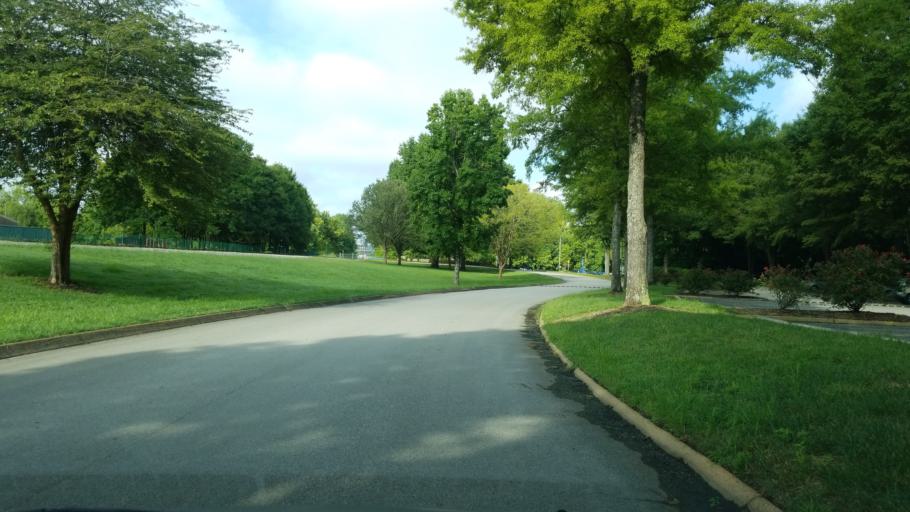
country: US
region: Tennessee
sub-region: Hamilton County
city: East Chattanooga
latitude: 35.0964
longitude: -85.2529
